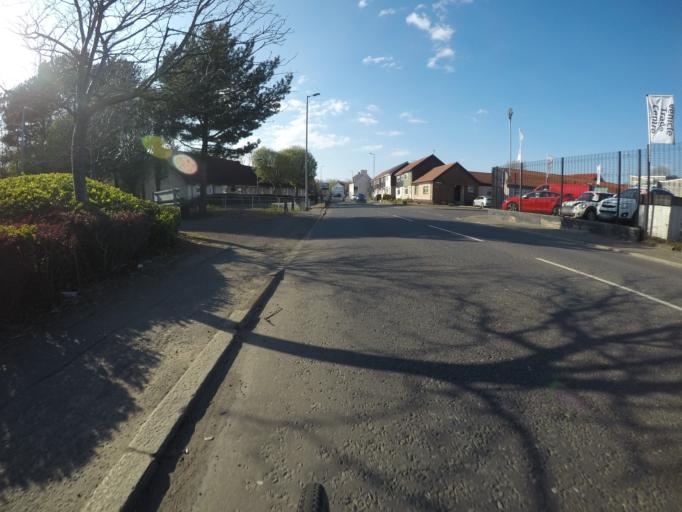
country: GB
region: Scotland
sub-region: North Ayrshire
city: Kilwinning
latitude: 55.6533
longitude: -4.6927
